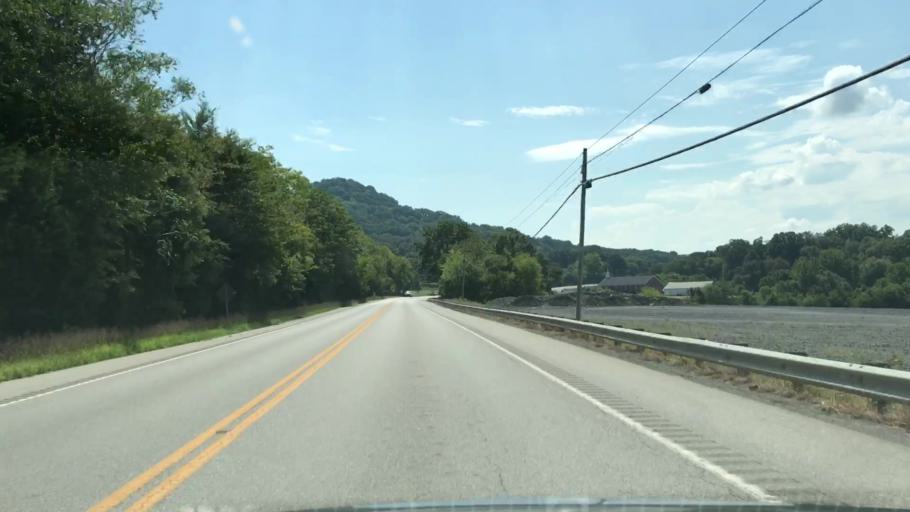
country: US
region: Tennessee
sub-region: Smith County
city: Carthage
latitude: 36.2906
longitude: -85.9948
